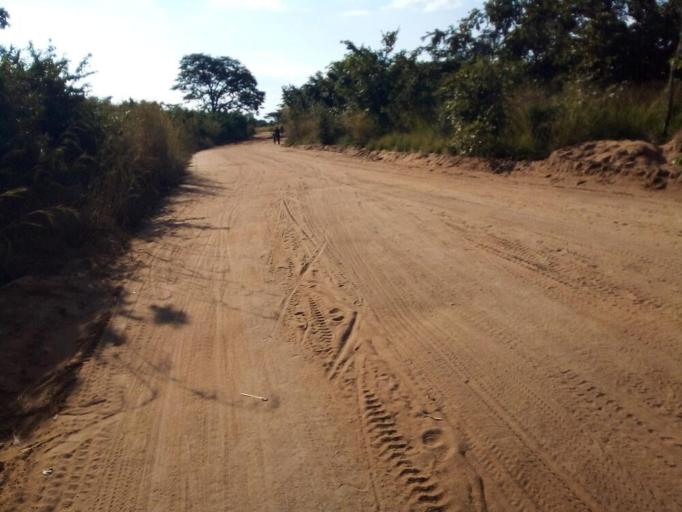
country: MZ
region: Zambezia
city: Quelimane
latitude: -17.5088
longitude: 36.8310
